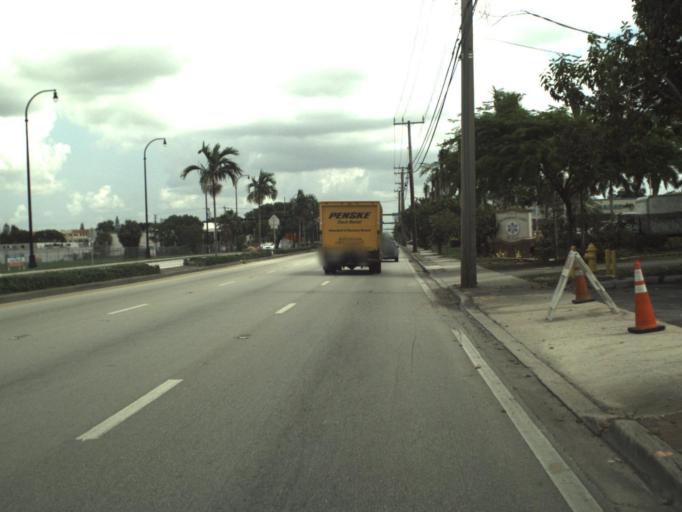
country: US
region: Florida
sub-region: Broward County
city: Lauderhill
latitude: 26.1510
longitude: -80.2027
